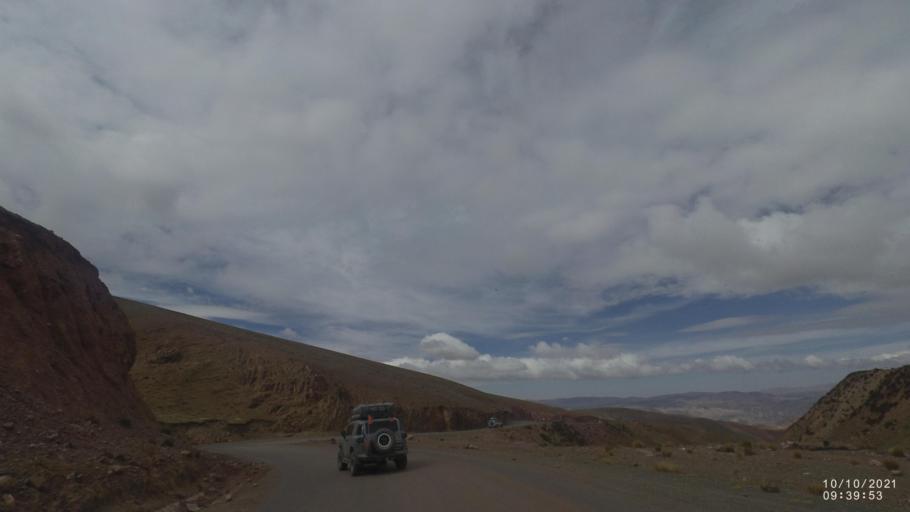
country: BO
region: La Paz
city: Quime
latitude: -17.1363
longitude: -67.3388
